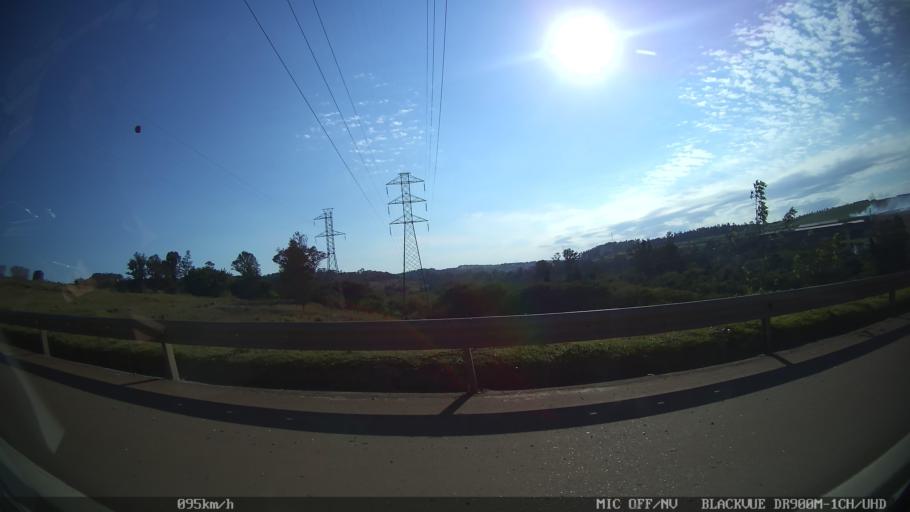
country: BR
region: Sao Paulo
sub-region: Piracicaba
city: Piracicaba
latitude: -22.7025
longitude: -47.6108
